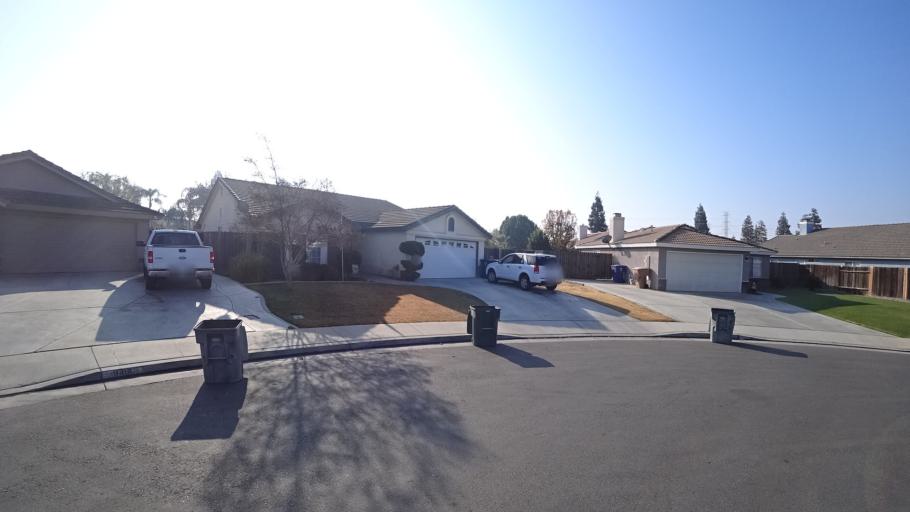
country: US
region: California
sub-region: Kern County
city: Greenacres
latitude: 35.3891
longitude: -119.1076
